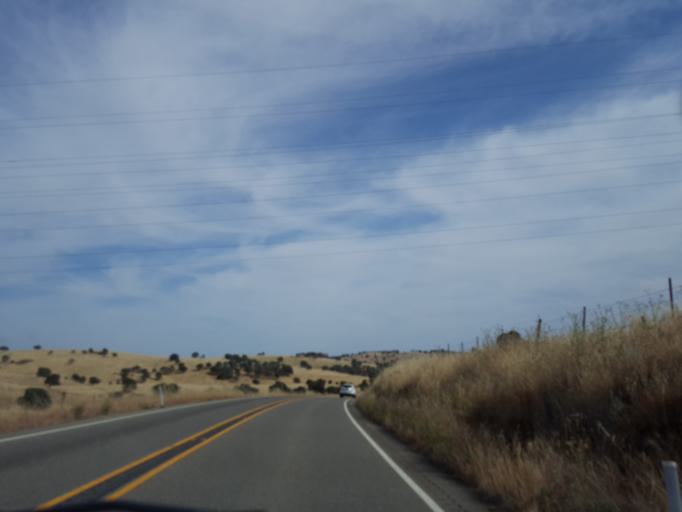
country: US
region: California
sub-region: Tuolumne County
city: Jamestown
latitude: 37.7882
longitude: -120.4643
